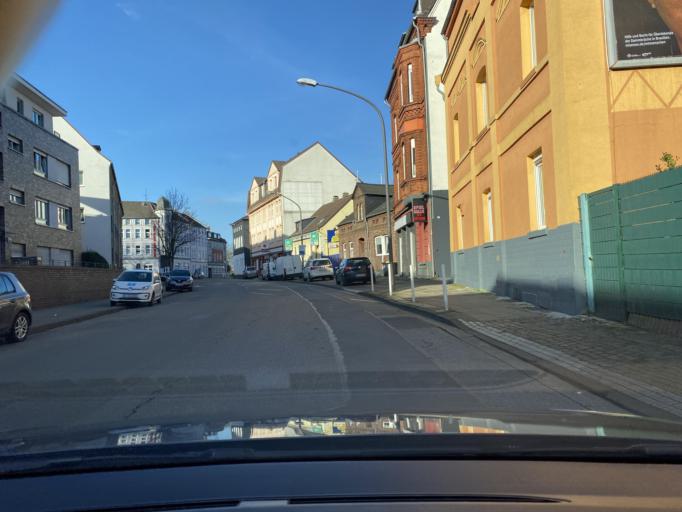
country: DE
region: North Rhine-Westphalia
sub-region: Regierungsbezirk Dusseldorf
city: Essen
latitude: 51.4922
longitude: 7.0534
